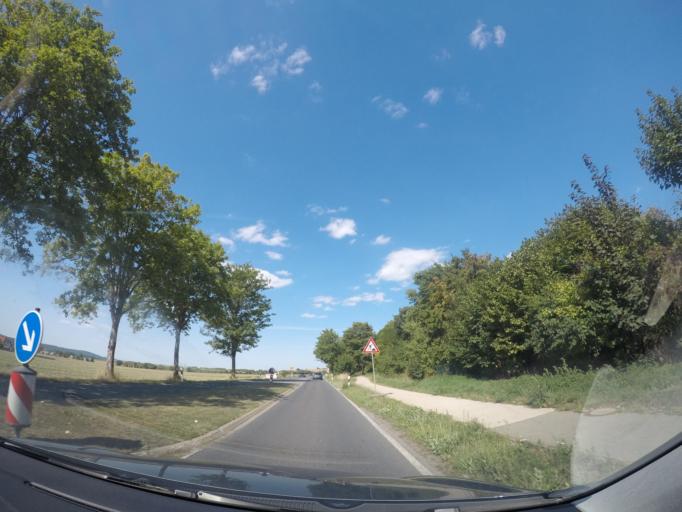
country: DE
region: Lower Saxony
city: Seesen
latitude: 51.8520
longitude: 10.1803
